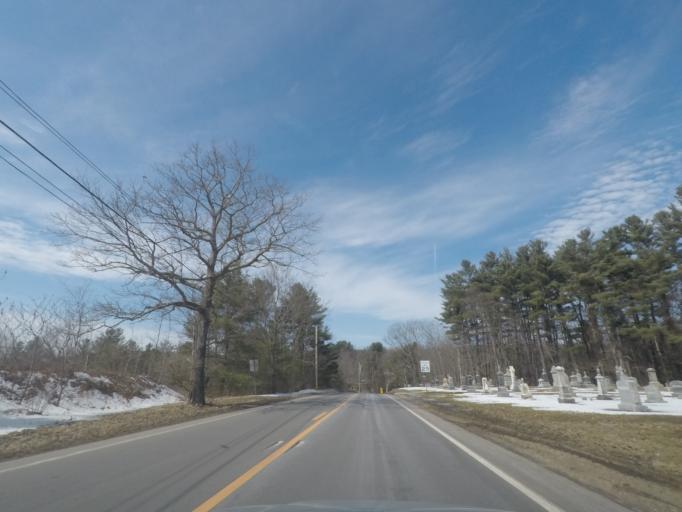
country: US
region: Massachusetts
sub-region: Berkshire County
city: West Stockbridge
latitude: 42.3506
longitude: -73.3844
